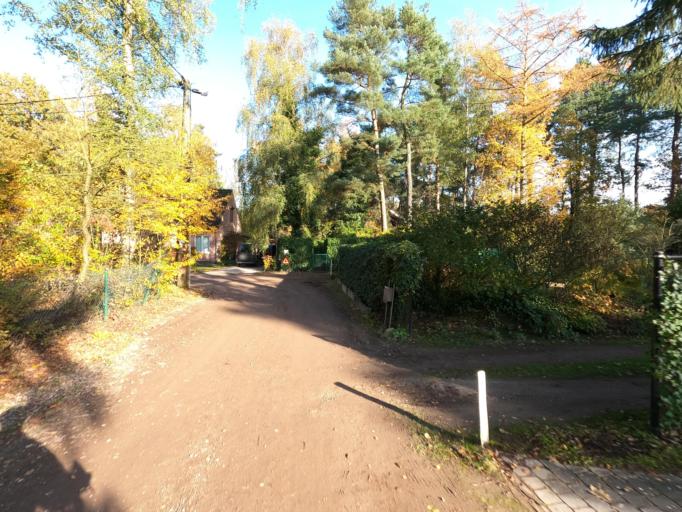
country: BE
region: Flanders
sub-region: Provincie Antwerpen
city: Wuustwezel
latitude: 51.3435
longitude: 4.5468
